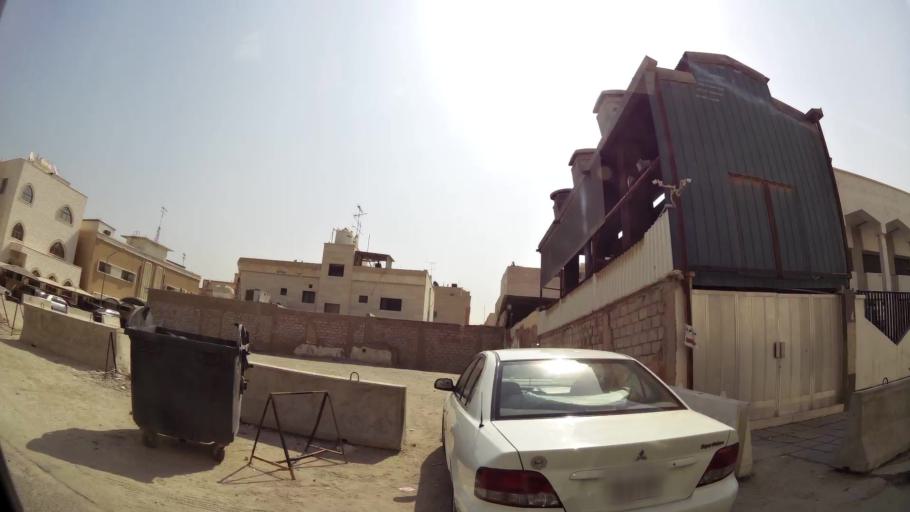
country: KW
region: Al Asimah
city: Ad Dasmah
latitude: 29.3580
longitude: 48.0156
